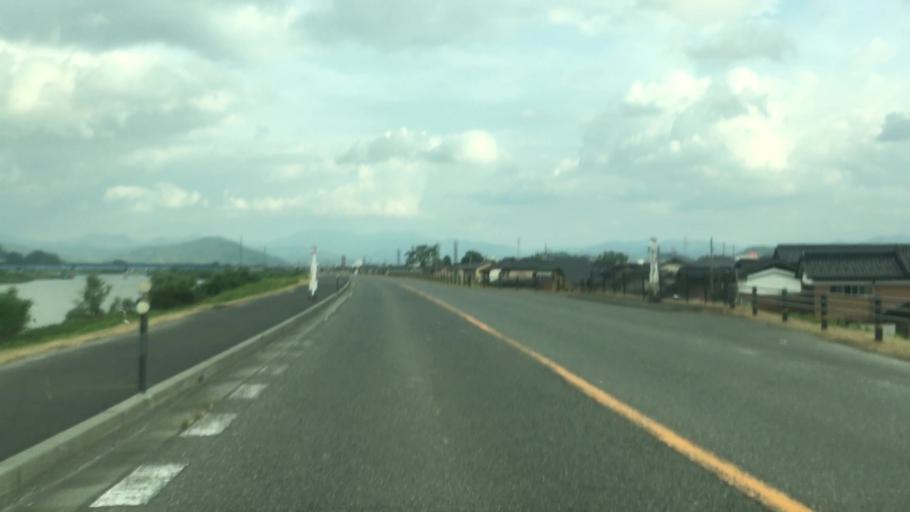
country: JP
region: Hyogo
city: Toyooka
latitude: 35.5630
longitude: 134.8128
